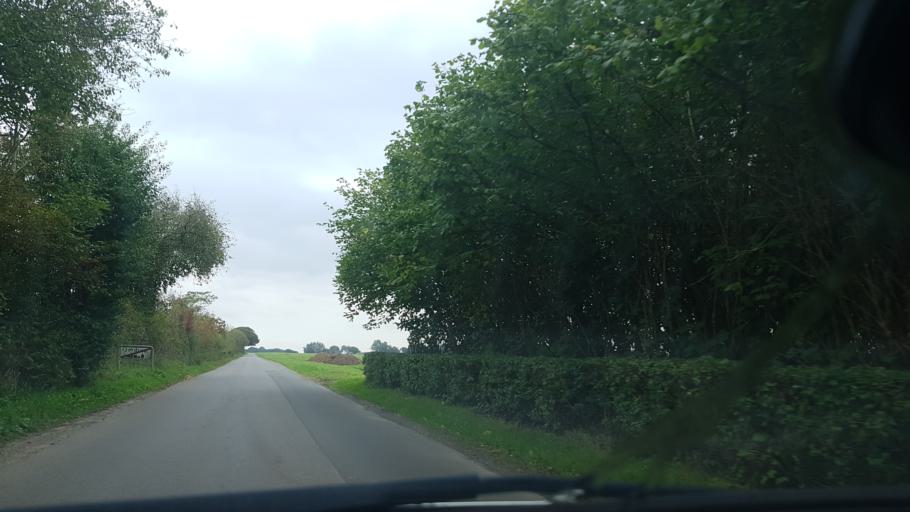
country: DK
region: South Denmark
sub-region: Vejle Kommune
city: Egtved
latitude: 55.5582
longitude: 9.3187
